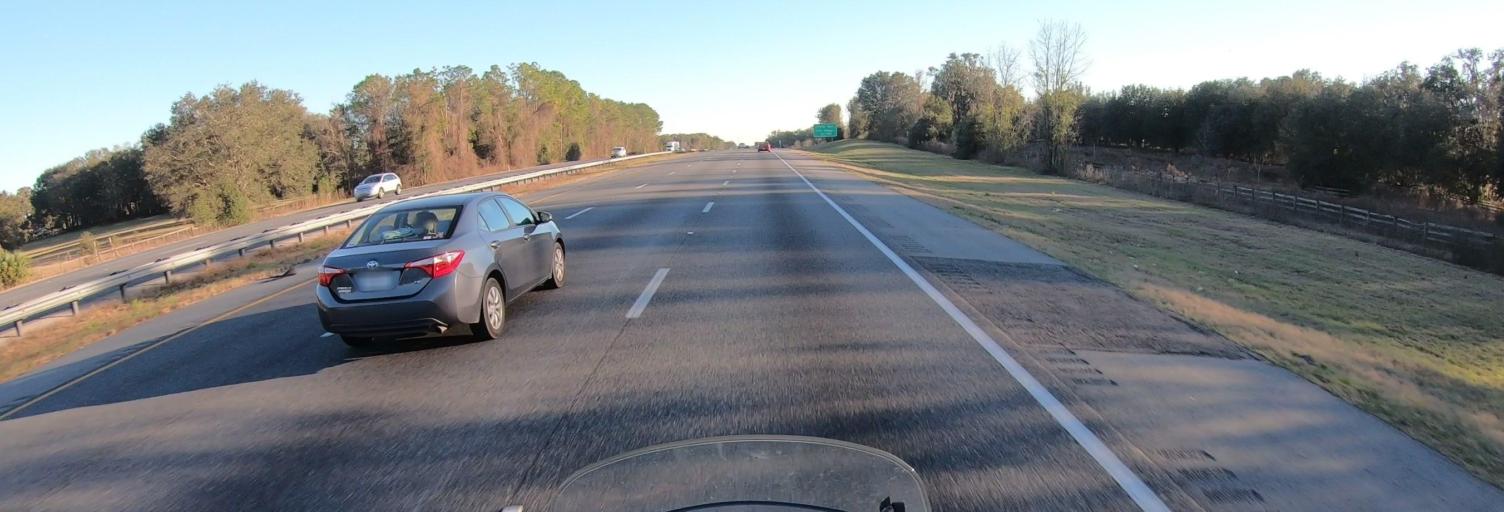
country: US
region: Florida
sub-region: Marion County
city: Ocala
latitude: 29.2886
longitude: -82.2017
